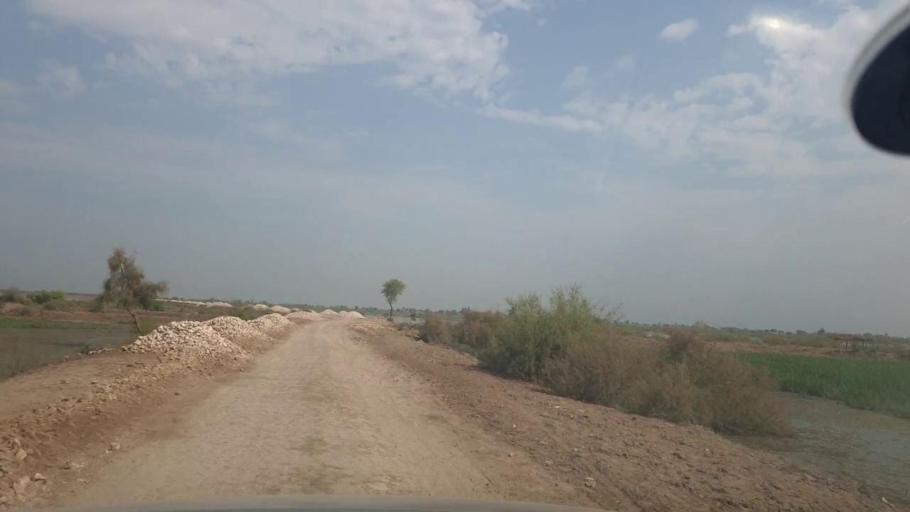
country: PK
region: Balochistan
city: Mehrabpur
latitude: 28.0782
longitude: 68.1011
